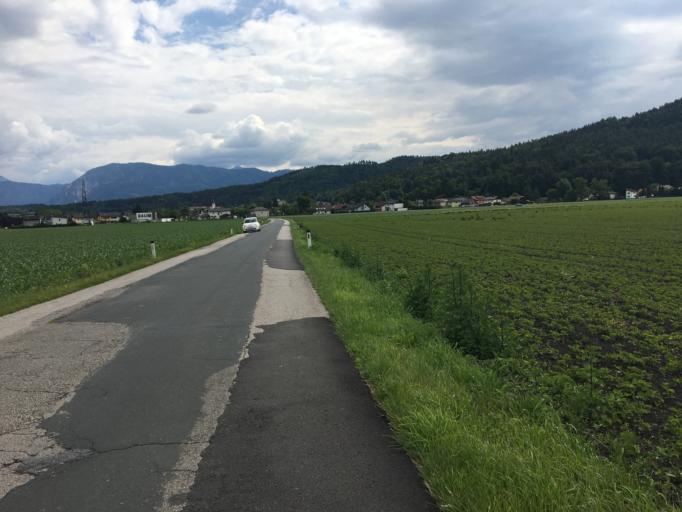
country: AT
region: Carinthia
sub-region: Klagenfurt am Woerthersee
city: Klagenfurt am Woerthersee
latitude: 46.6041
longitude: 14.2738
